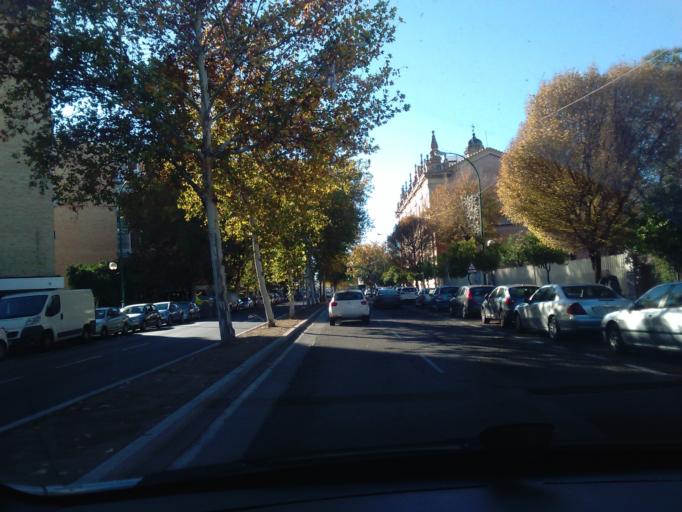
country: ES
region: Andalusia
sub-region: Provincia de Sevilla
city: Sevilla
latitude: 37.3841
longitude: -5.9655
